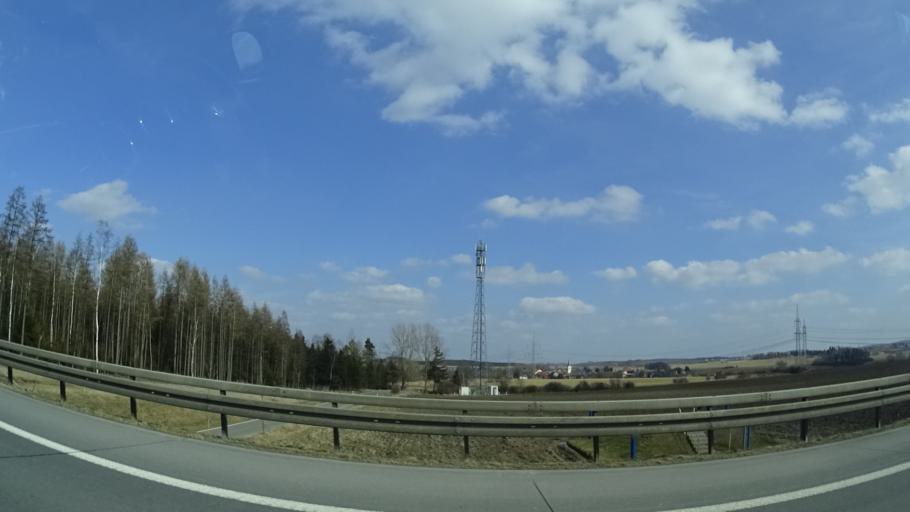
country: DE
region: Thuringia
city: Pormitz
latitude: 50.6160
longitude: 11.7923
